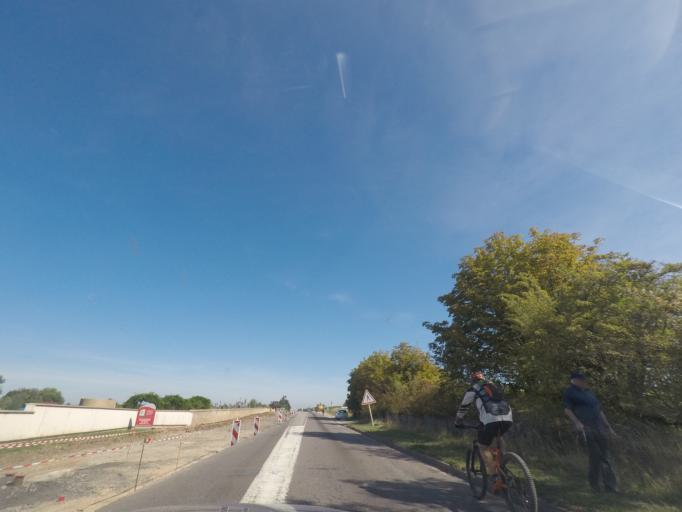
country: FR
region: Lorraine
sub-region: Departement de la Moselle
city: Hettange-Grande
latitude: 49.4099
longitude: 6.1539
